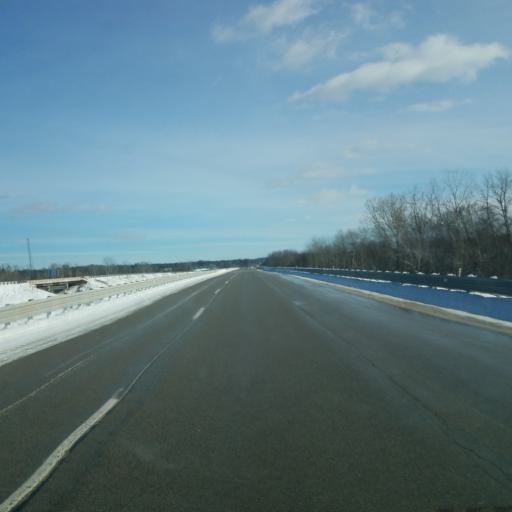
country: US
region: Michigan
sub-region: Clare County
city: Clare
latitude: 43.8664
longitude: -84.9030
